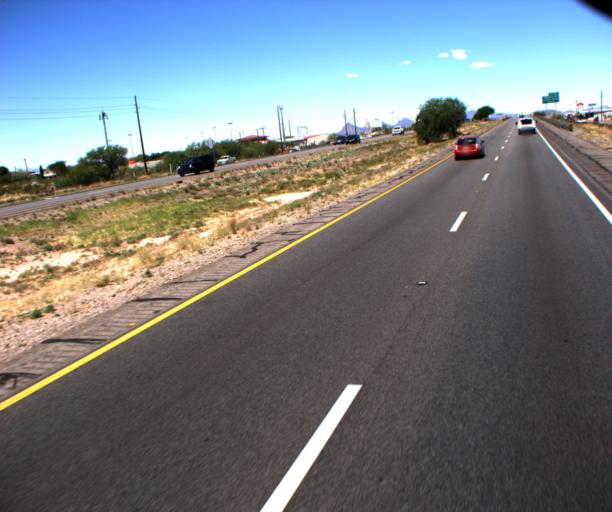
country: US
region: Arizona
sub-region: Pima County
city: Summit
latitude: 32.1235
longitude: -110.8720
